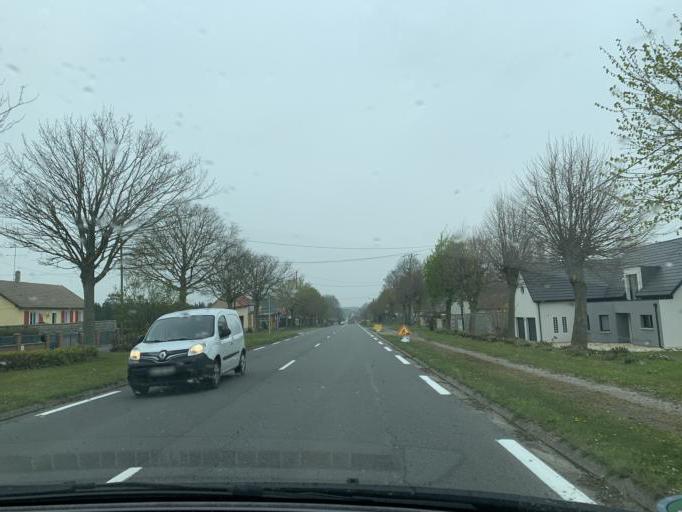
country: FR
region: Picardie
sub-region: Departement de la Somme
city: Nouvion
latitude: 50.2032
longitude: 1.7872
